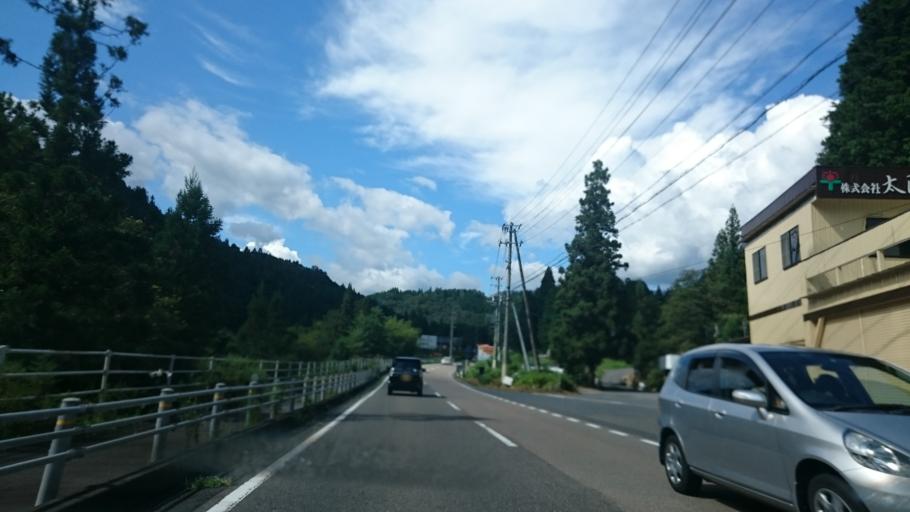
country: JP
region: Gifu
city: Nakatsugawa
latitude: 35.6018
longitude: 137.4640
